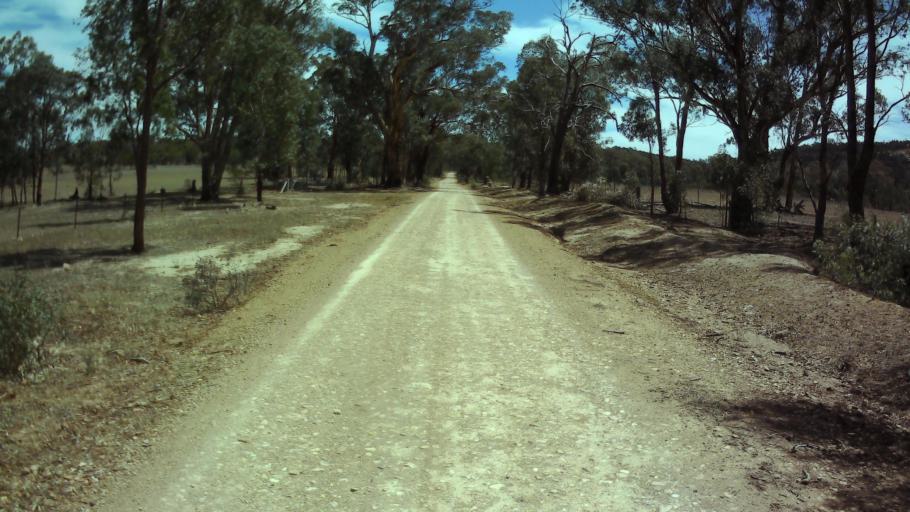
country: AU
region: New South Wales
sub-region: Weddin
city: Grenfell
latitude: -33.7469
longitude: 148.1965
